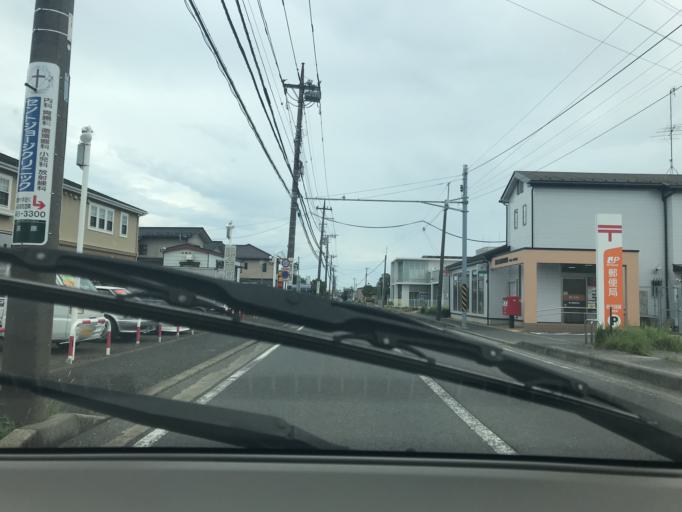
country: JP
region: Kanagawa
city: Fujisawa
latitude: 35.3897
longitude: 139.4400
